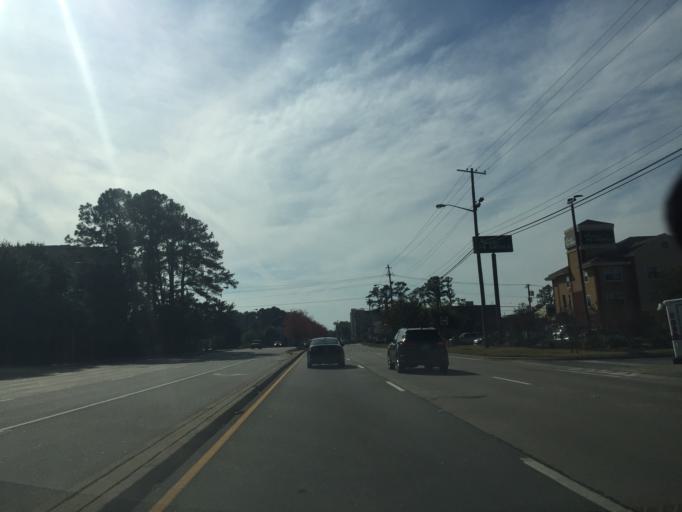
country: US
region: Georgia
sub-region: Chatham County
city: Savannah
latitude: 32.0261
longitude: -81.1090
